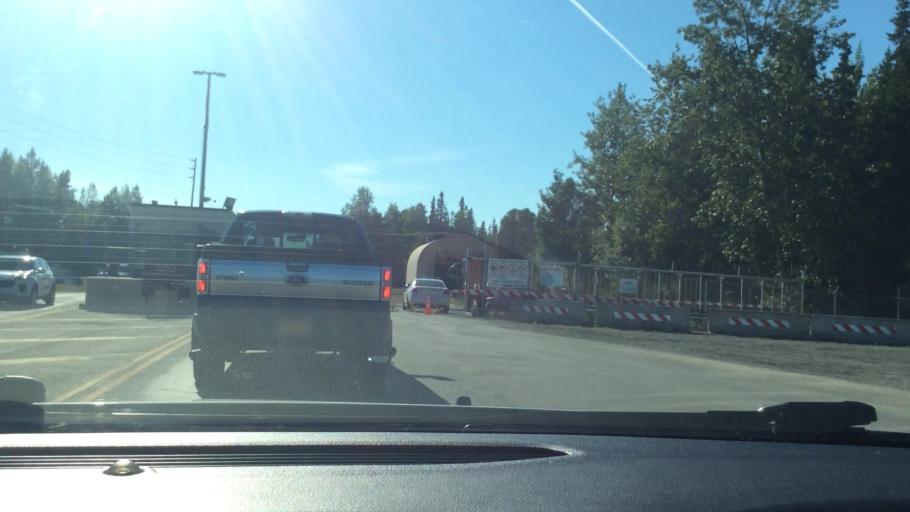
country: US
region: Alaska
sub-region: Anchorage Municipality
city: Elmendorf Air Force Base
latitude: 61.2314
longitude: -149.7463
